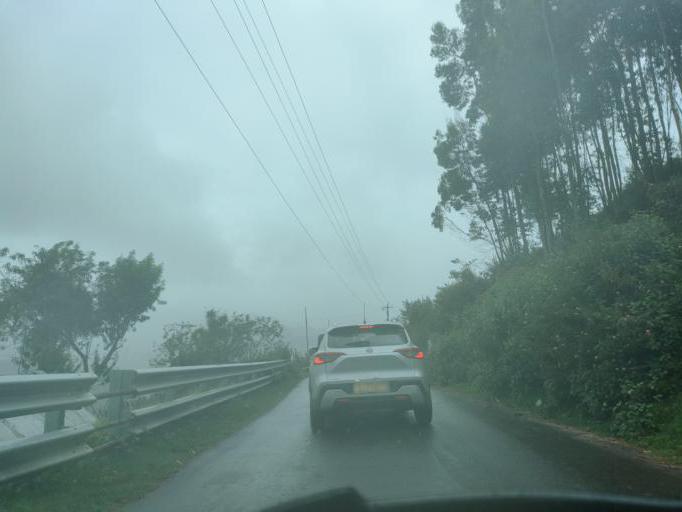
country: IN
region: Tamil Nadu
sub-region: Dindigul
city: Kodaikanal
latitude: 10.2360
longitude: 77.3498
